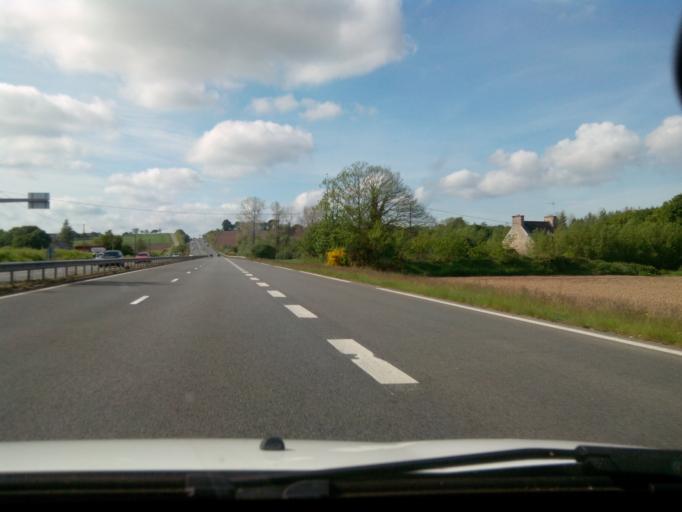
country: FR
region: Brittany
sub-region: Departement des Cotes-d'Armor
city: Cavan
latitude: 48.6927
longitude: -3.3698
